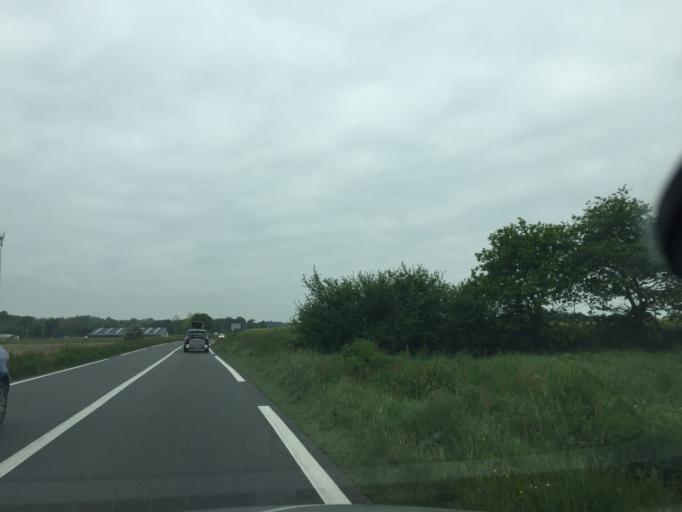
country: FR
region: Brittany
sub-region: Departement des Cotes-d'Armor
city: Henanbihen
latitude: 48.5308
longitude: -2.4199
